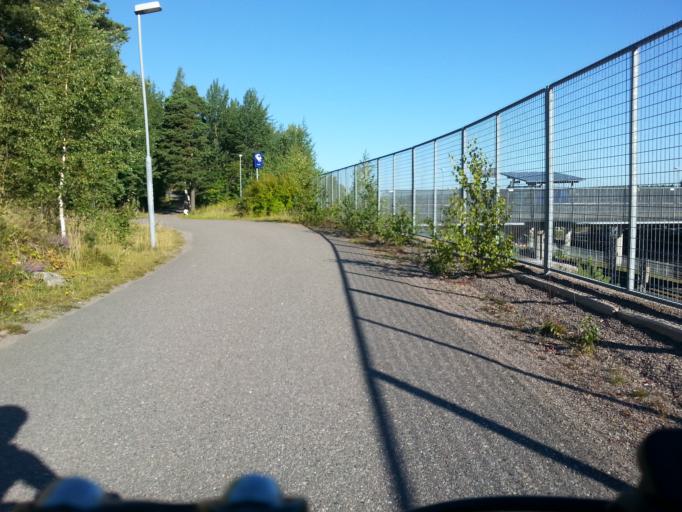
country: FI
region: Uusimaa
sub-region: Helsinki
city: Helsinki
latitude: 60.2063
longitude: 24.9232
